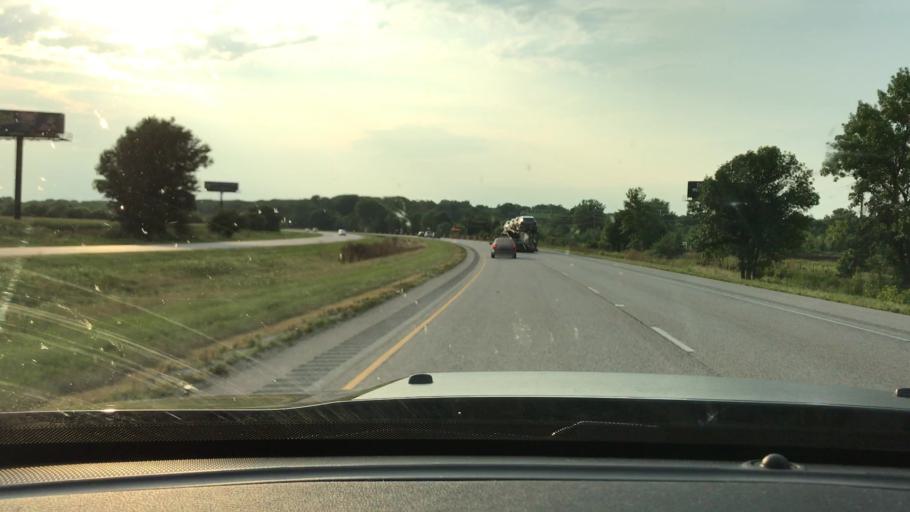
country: US
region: Illinois
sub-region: Henry County
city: Green Rock
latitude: 41.4612
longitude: -90.3825
